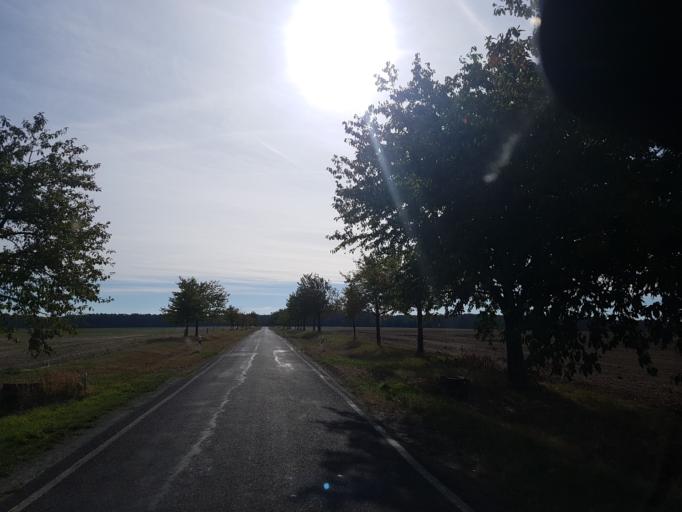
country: DE
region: Brandenburg
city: Ihlow
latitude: 51.7993
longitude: 13.3114
